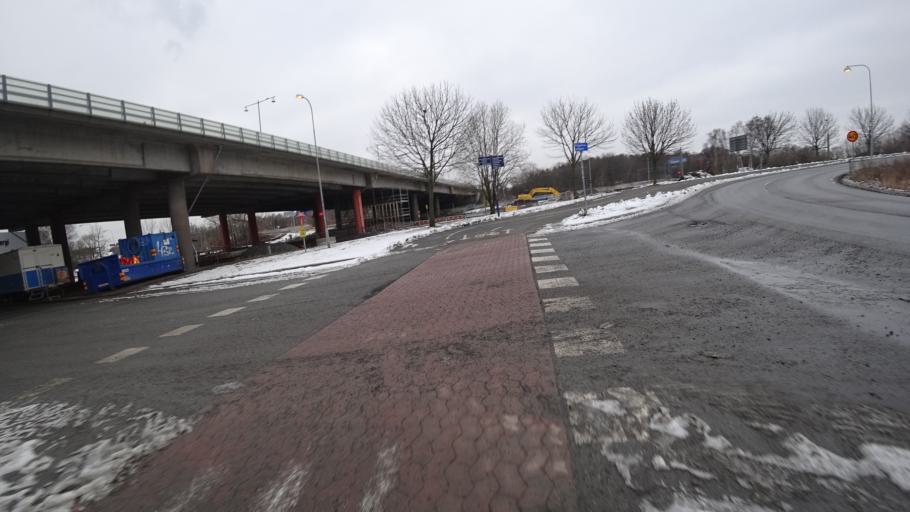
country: SE
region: Vaestra Goetaland
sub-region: Goteborg
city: Majorna
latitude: 57.6981
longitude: 11.8970
